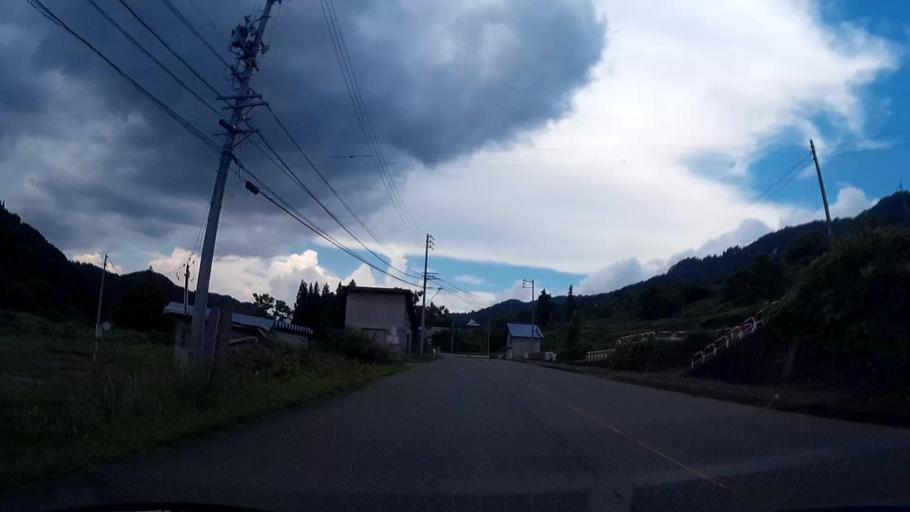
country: JP
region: Nagano
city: Iiyama
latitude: 36.9854
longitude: 138.5390
